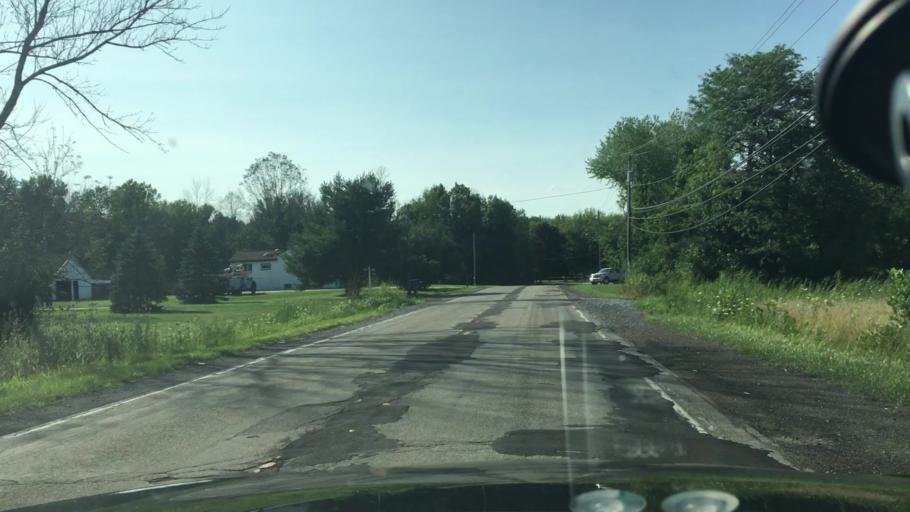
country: US
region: New York
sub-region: Erie County
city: Angola
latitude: 42.6241
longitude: -79.0248
